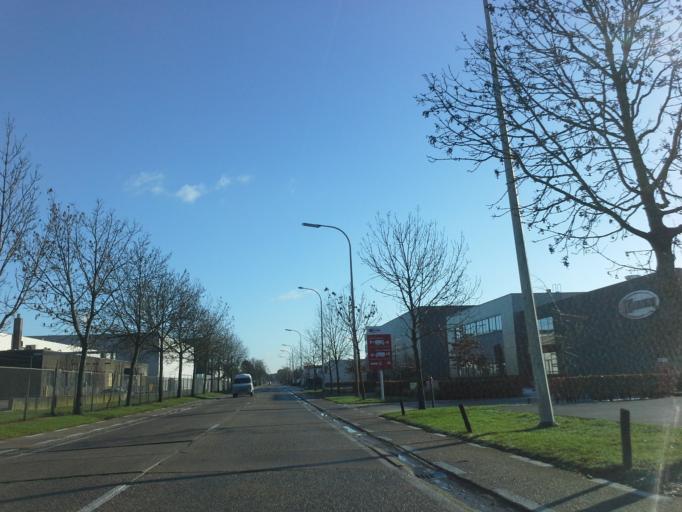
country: BE
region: Flanders
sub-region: Provincie Antwerpen
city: Herentals
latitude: 51.1656
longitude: 4.7948
